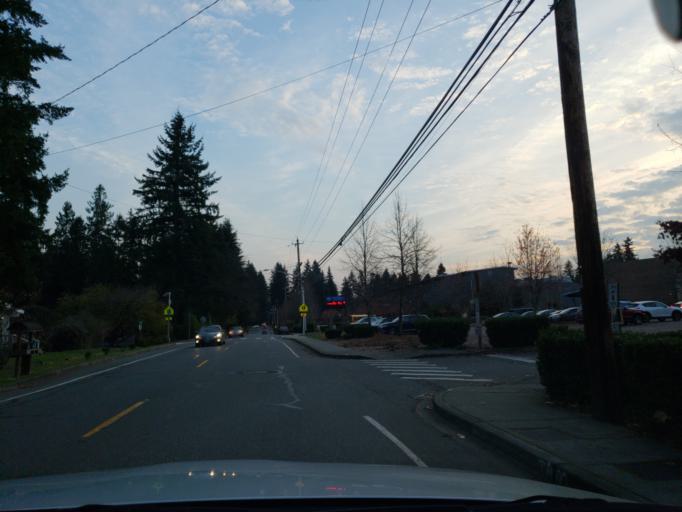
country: US
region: Washington
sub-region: King County
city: Bothell
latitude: 47.7613
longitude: -122.2177
